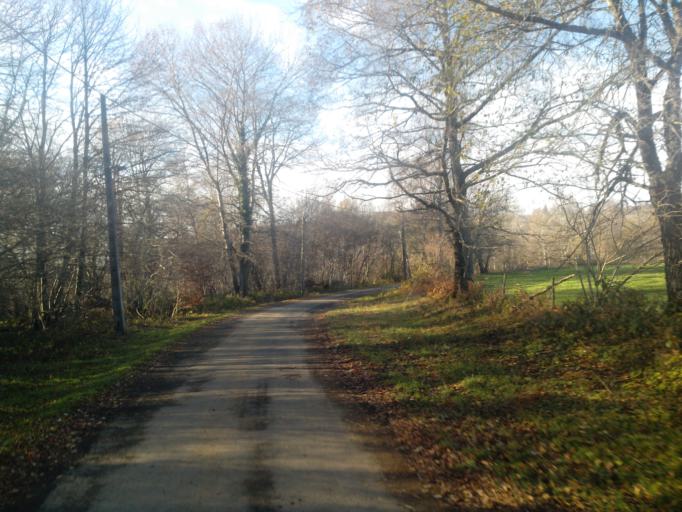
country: FR
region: Limousin
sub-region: Departement de la Correze
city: Bort-les-Orgues
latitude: 45.3966
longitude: 2.4796
